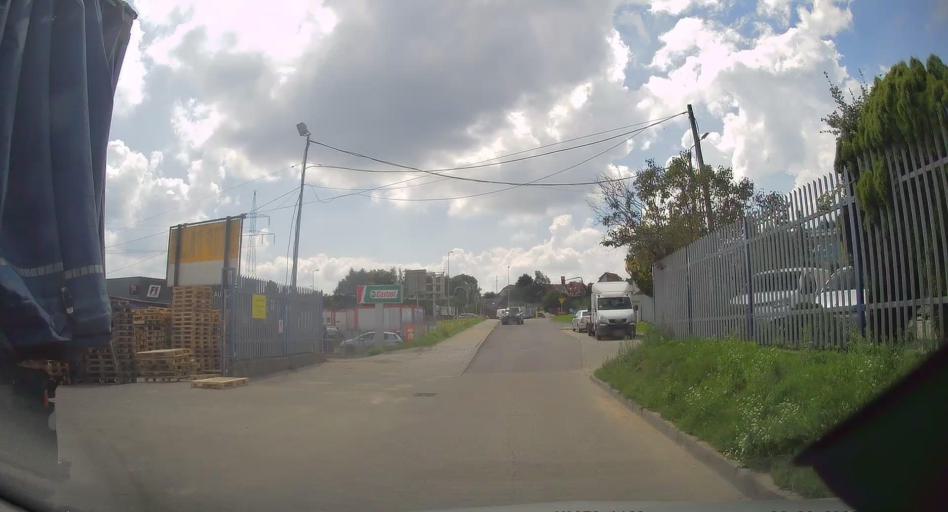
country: PL
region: Lesser Poland Voivodeship
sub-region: Powiat wielicki
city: Wieliczka
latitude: 50.0022
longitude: 20.0267
